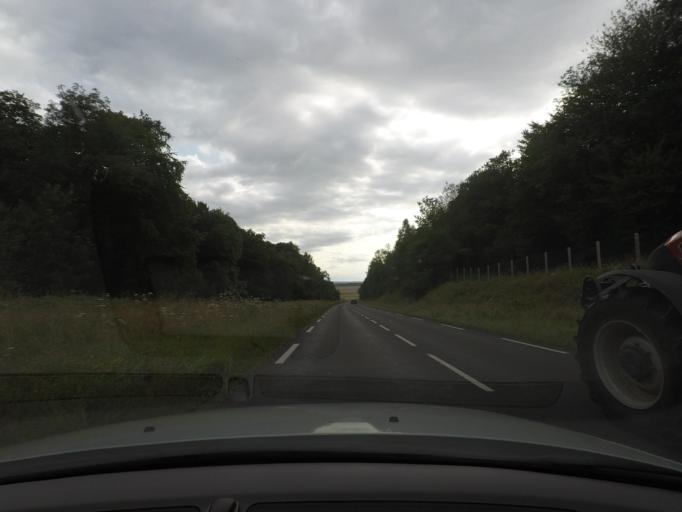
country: FR
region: Haute-Normandie
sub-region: Departement de la Seine-Maritime
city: Ymare
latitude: 49.3528
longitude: 1.1695
